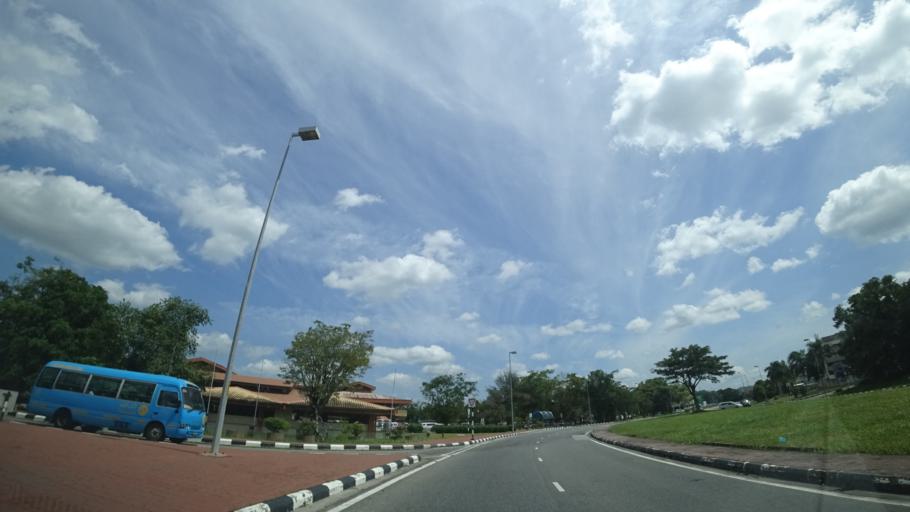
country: BN
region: Brunei and Muara
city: Bandar Seri Begawan
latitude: 4.9043
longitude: 114.9171
